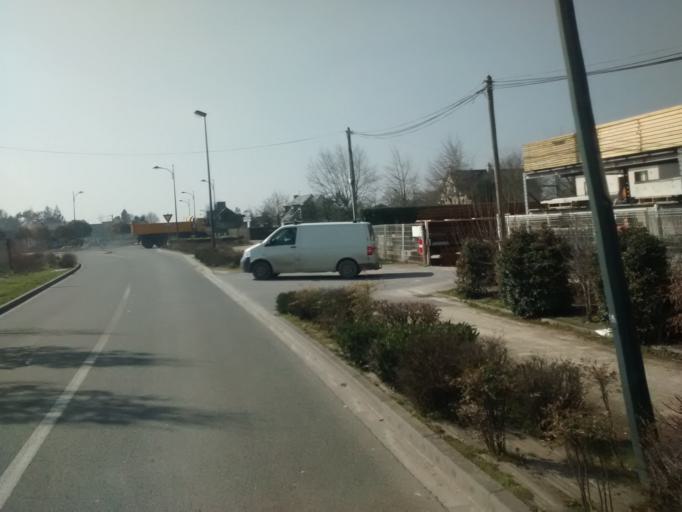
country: FR
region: Brittany
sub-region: Departement d'Ille-et-Vilaine
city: Plelan-le-Grand
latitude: 48.0066
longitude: -2.0869
